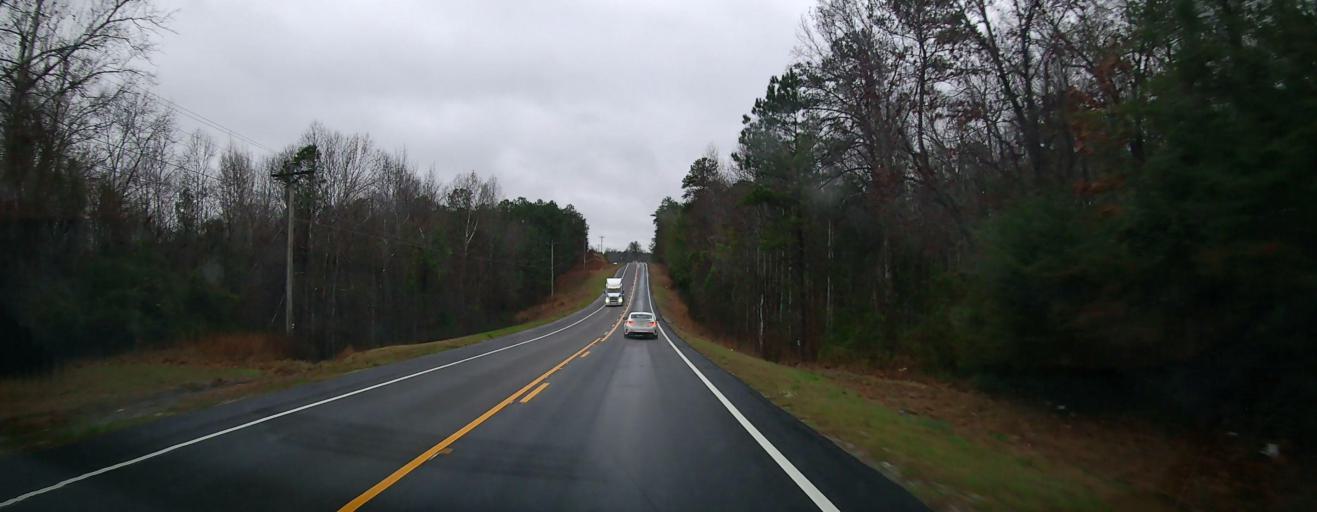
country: US
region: Alabama
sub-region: Chilton County
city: Clanton
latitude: 32.6934
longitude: -86.7980
